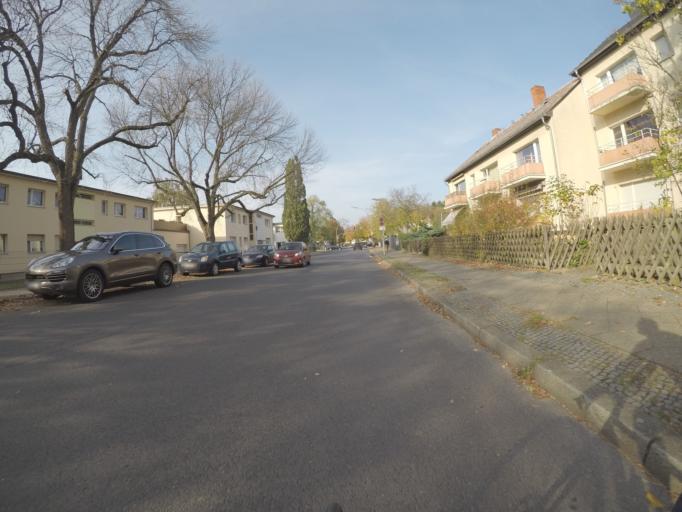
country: DE
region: Berlin
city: Britz
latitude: 52.4202
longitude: 13.4282
